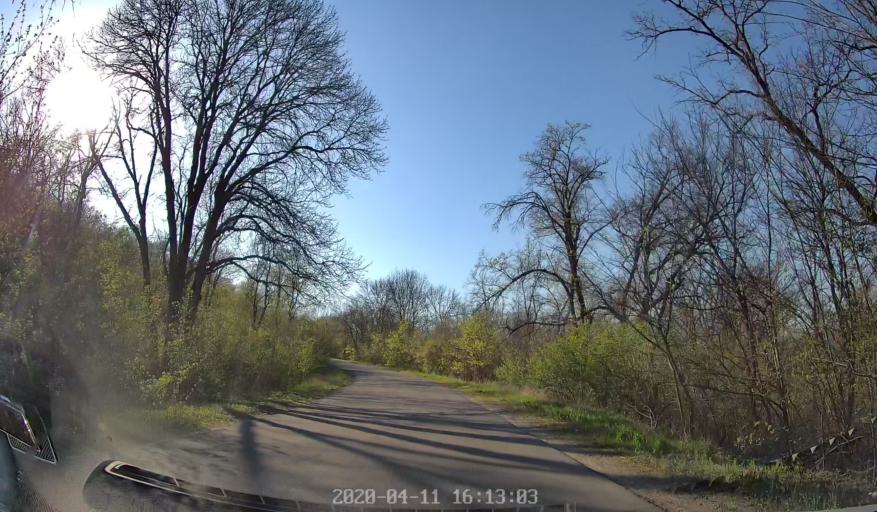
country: MD
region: Chisinau
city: Vadul lui Voda
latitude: 47.0714
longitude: 29.1159
